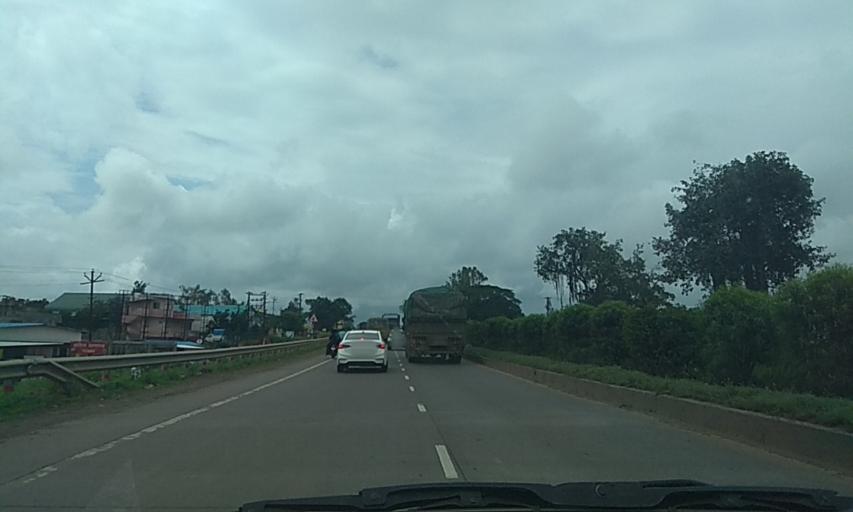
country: IN
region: Maharashtra
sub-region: Kolhapur
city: Kolhapur
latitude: 16.6464
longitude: 74.2752
